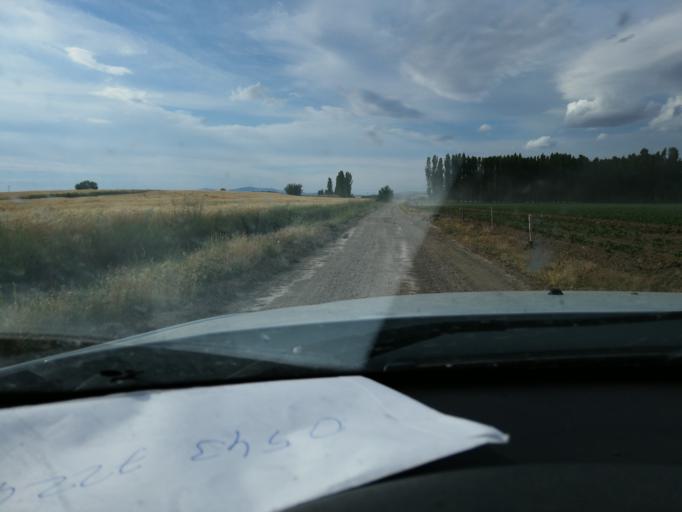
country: TR
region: Kirsehir
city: Kirsehir
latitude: 39.0011
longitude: 34.1242
